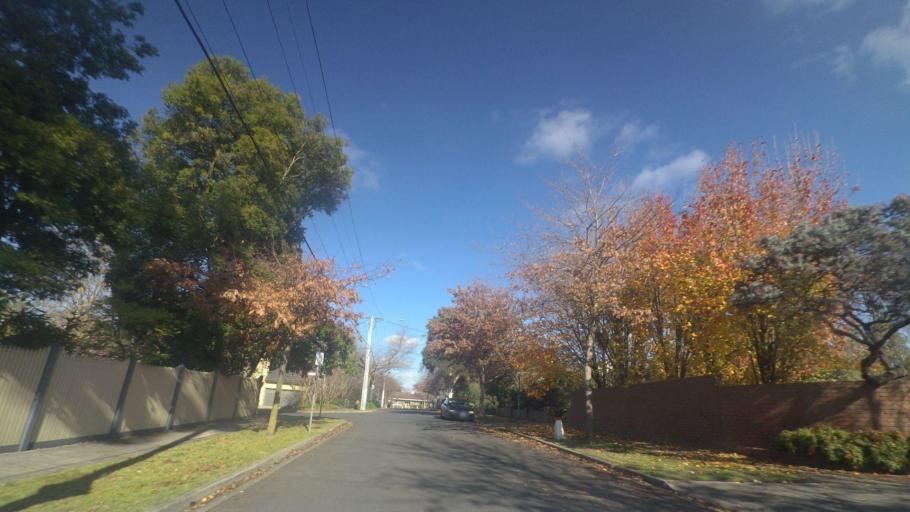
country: AU
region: Victoria
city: Mont Albert
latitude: -37.8126
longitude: 145.1105
